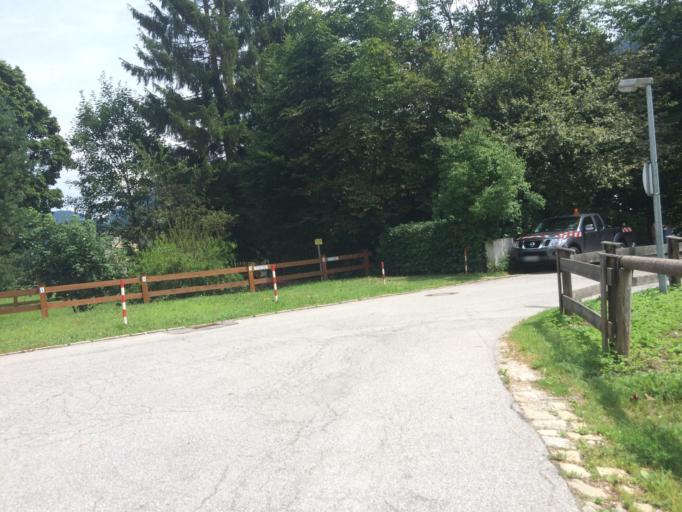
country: DE
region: Bavaria
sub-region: Upper Bavaria
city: Berchtesgaden
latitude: 47.6341
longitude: 13.0057
